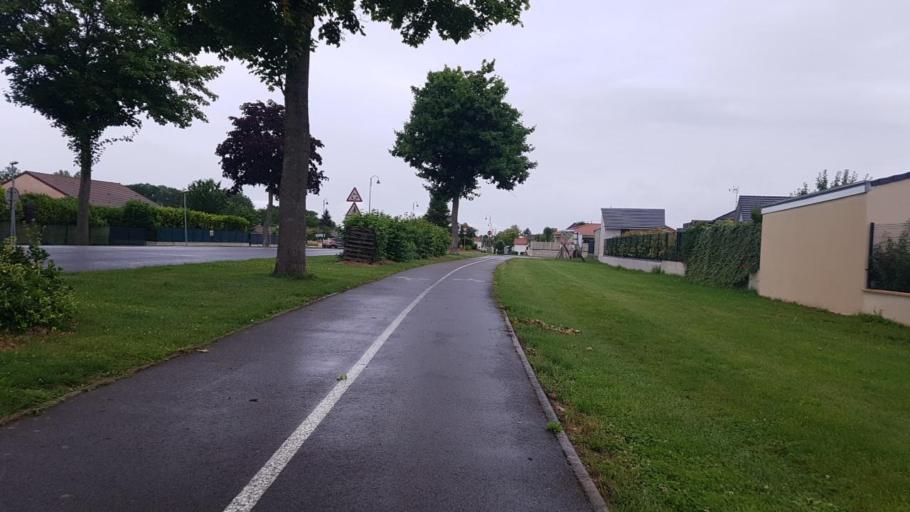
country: FR
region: Champagne-Ardenne
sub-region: Departement de la Marne
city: Sarry
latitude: 48.9138
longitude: 4.4156
